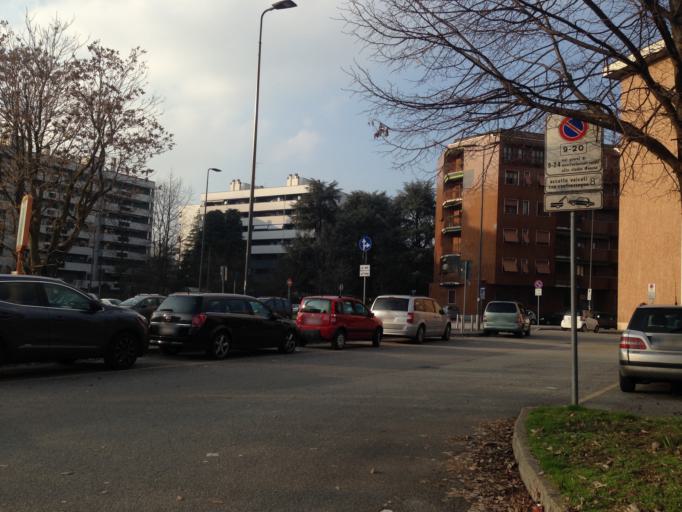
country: IT
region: Lombardy
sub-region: Citta metropolitana di Milano
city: Cesano Boscone
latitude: 45.4734
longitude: 9.1067
